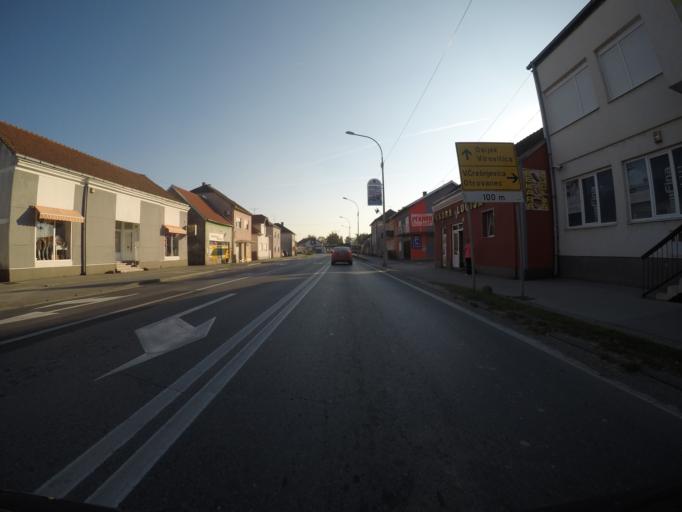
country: HR
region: Virovitick-Podravska
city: Pitomaca
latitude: 45.9486
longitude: 17.2321
